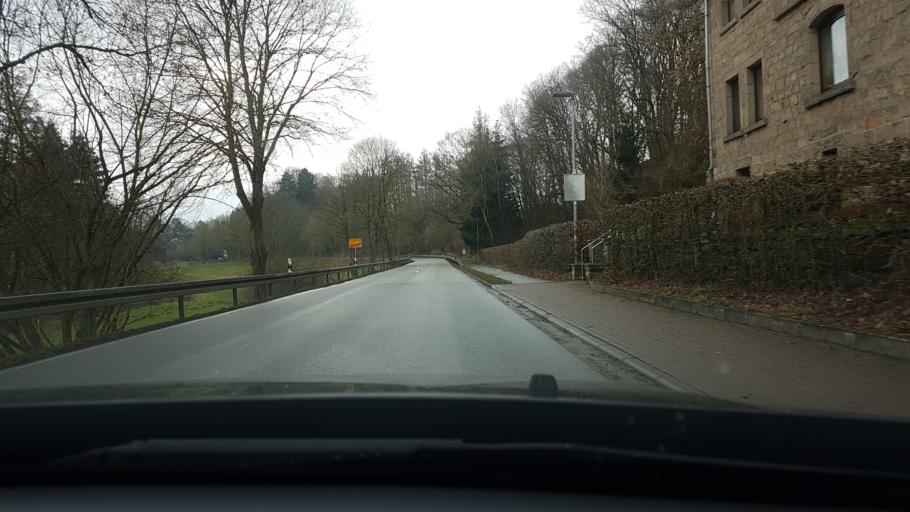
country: DE
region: North Rhine-Westphalia
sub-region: Regierungsbezirk Detmold
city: Willebadessen
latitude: 51.5055
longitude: 8.9992
